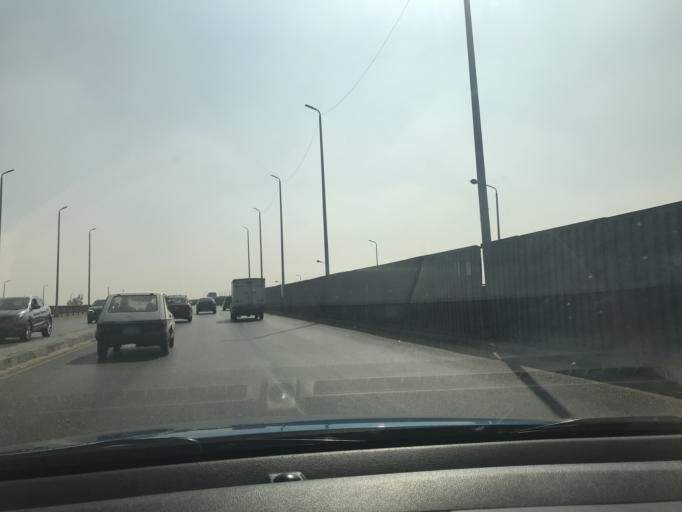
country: EG
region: Muhafazat al Qalyubiyah
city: Al Khankah
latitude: 30.1391
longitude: 31.3981
